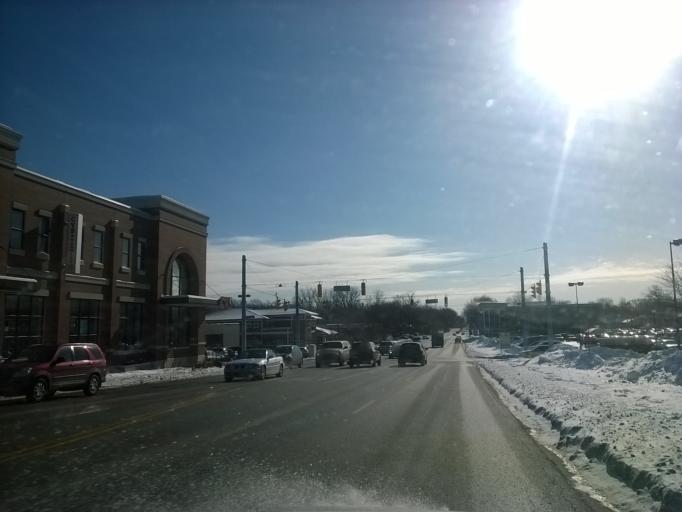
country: US
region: Indiana
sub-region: Hamilton County
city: Carmel
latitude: 39.9589
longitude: -86.1269
